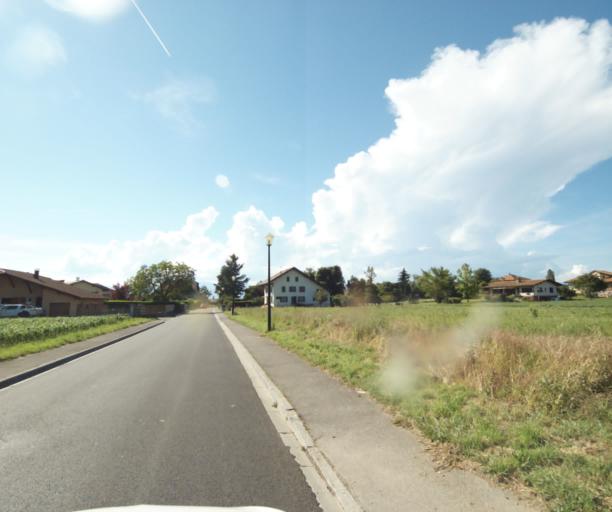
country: FR
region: Rhone-Alpes
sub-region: Departement de la Haute-Savoie
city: Massongy
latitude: 46.3198
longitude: 6.3284
